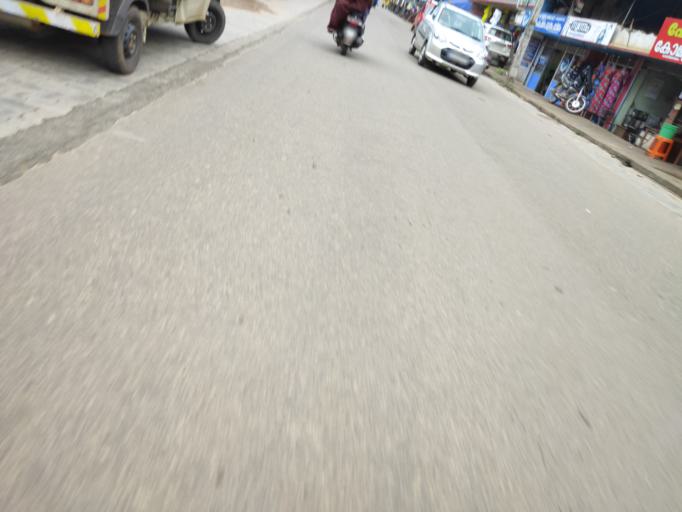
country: IN
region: Kerala
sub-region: Malappuram
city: Manjeri
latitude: 11.1906
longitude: 76.2585
